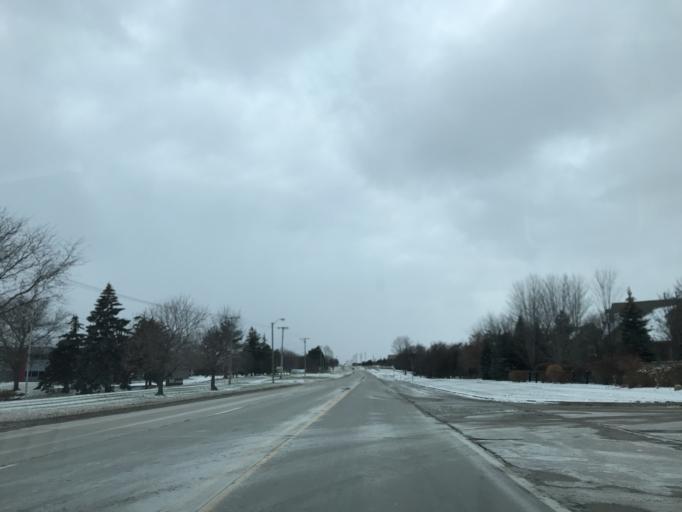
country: US
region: Michigan
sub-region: Wayne County
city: Plymouth
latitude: 42.3955
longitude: -83.4880
